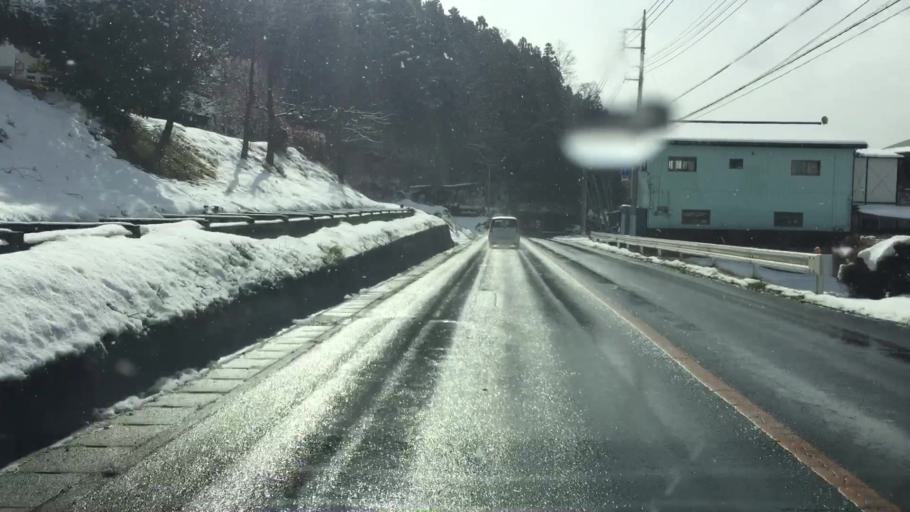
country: JP
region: Gunma
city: Numata
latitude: 36.6753
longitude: 139.0630
